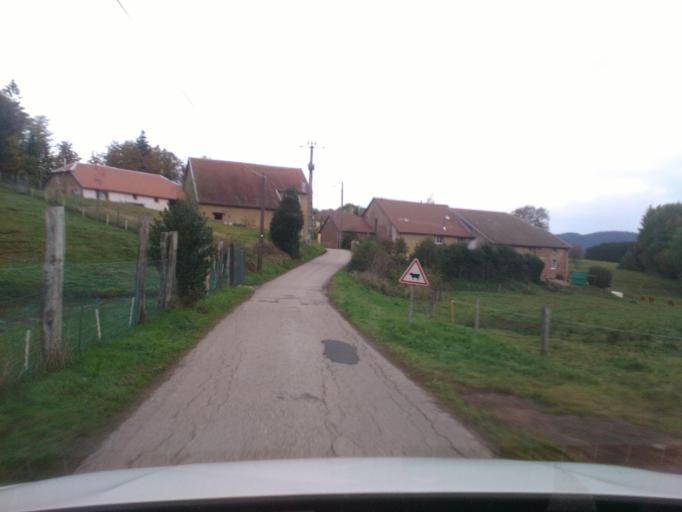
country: FR
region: Lorraine
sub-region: Departement des Vosges
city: Senones
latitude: 48.3790
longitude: 7.0218
